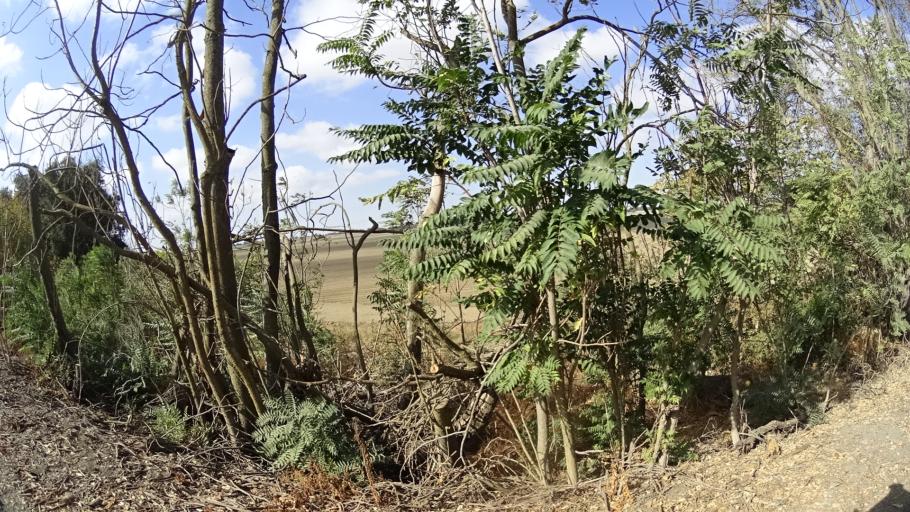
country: US
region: California
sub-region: Yolo County
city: Woodland
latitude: 38.7550
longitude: -121.6749
